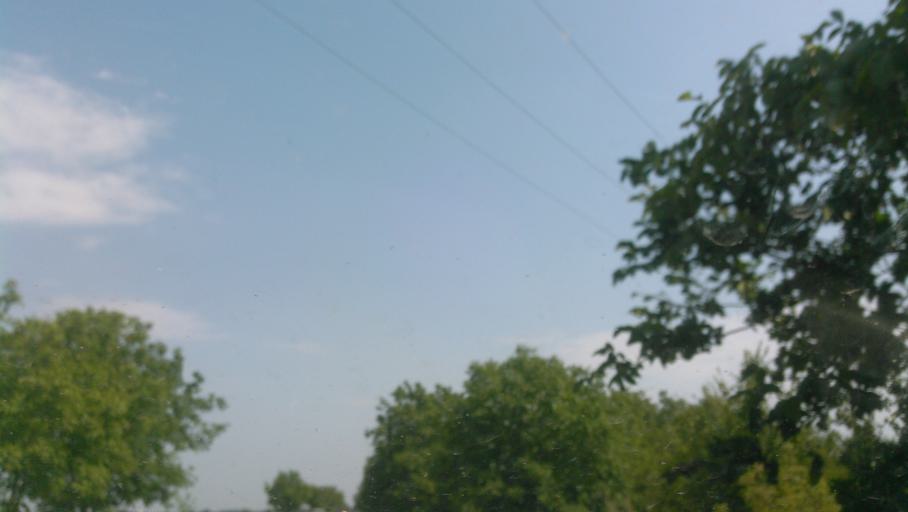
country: SK
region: Trnavsky
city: Dunajska Streda
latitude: 48.0466
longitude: 17.4867
